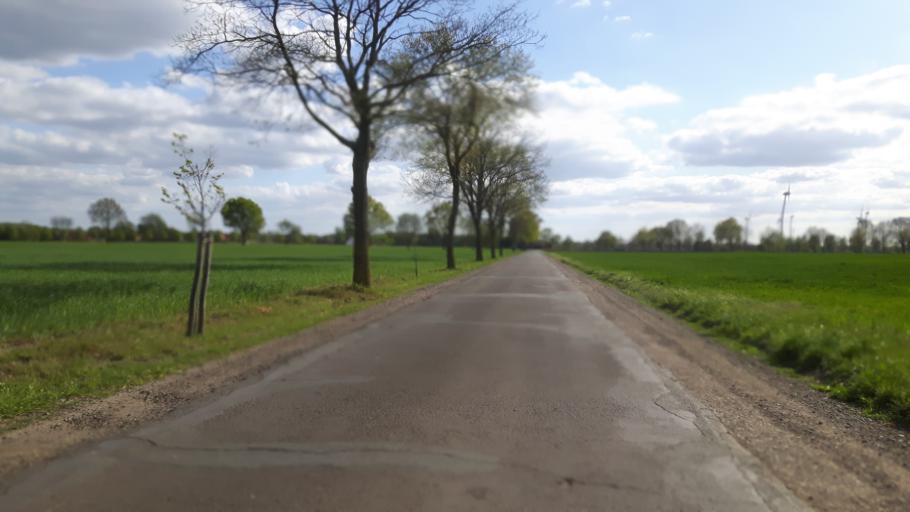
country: DE
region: Lower Saxony
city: Kirchseelte
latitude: 53.0017
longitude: 8.6913
